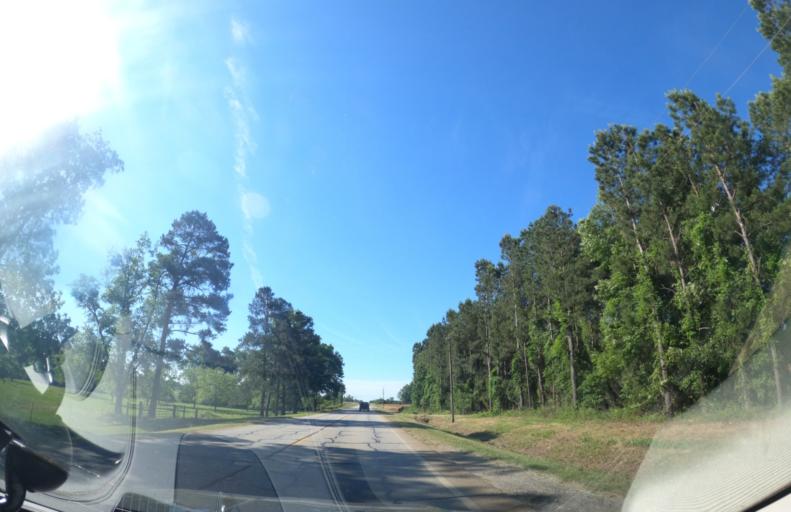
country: US
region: Georgia
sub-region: Jefferson County
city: Wrens
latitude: 33.2391
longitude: -82.3846
